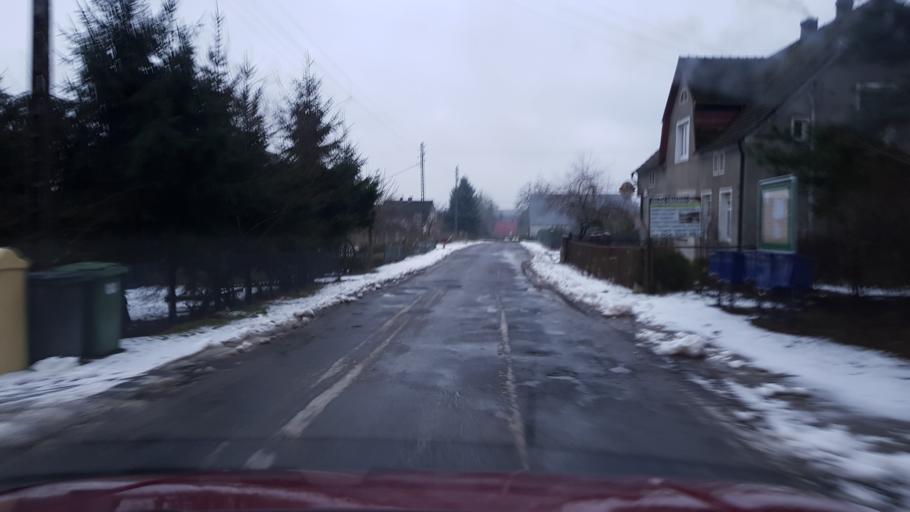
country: PL
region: West Pomeranian Voivodeship
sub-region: Powiat goleniowski
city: Mosty
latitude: 53.4995
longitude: 14.8979
